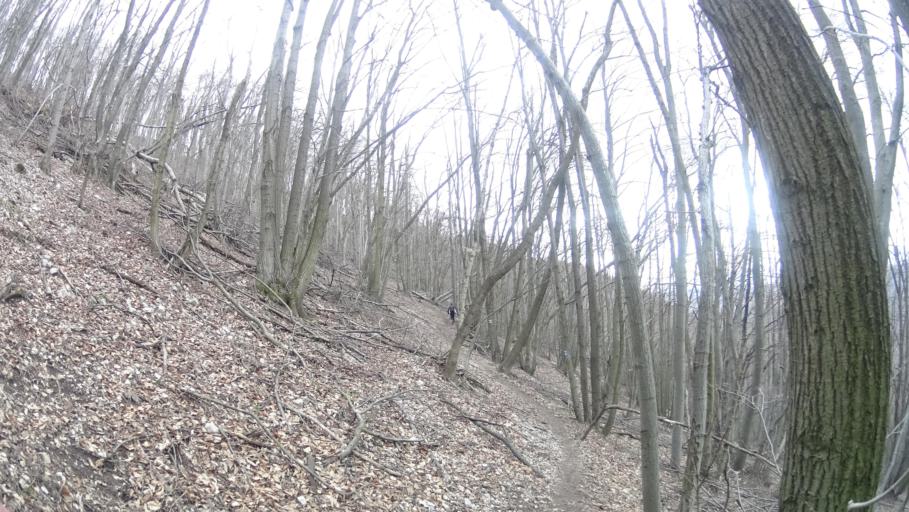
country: HU
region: Pest
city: Kosd
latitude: 47.8366
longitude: 19.1502
